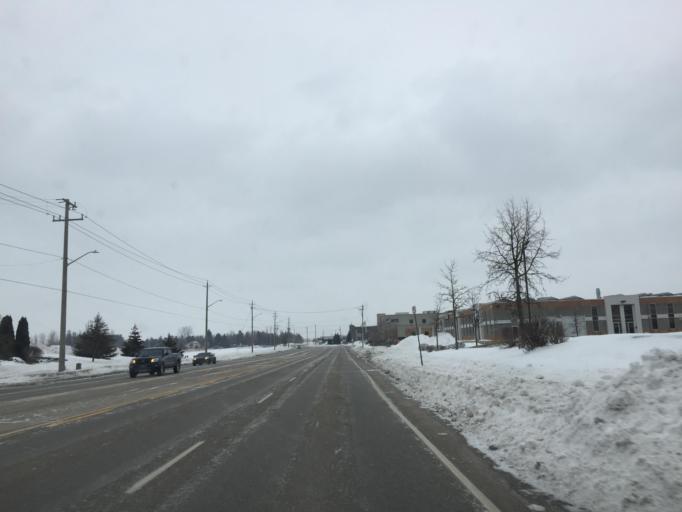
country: CA
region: Ontario
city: Waterloo
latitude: 43.4717
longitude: -80.4487
